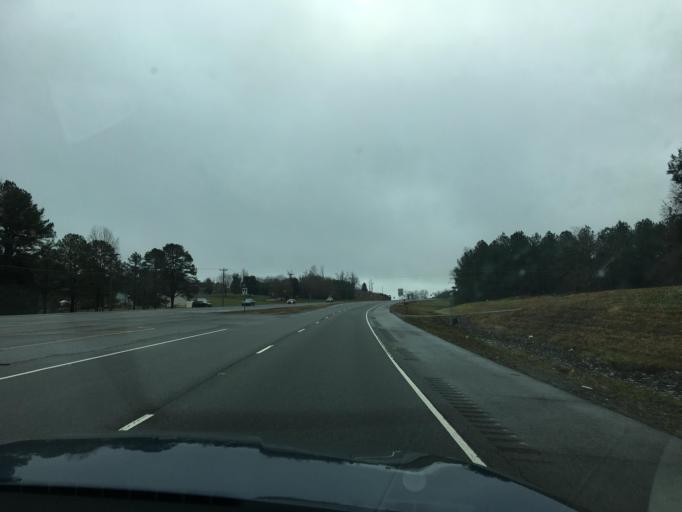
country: US
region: Tennessee
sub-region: McMinn County
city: Etowah
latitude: 35.3815
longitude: -84.5602
